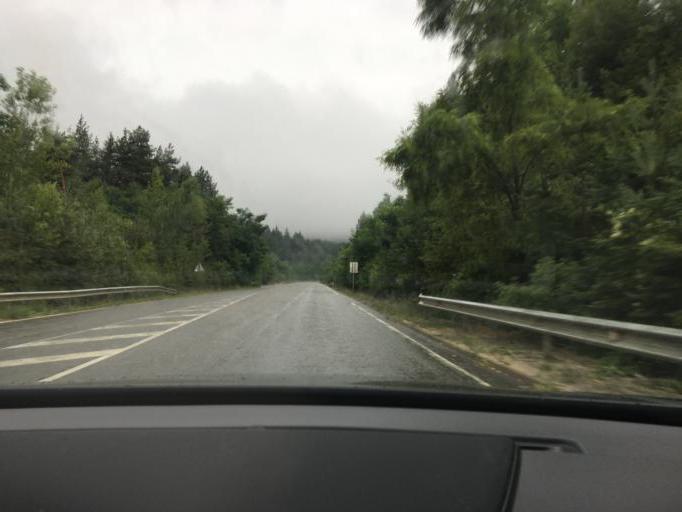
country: BG
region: Kyustendil
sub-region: Obshtina Kyustendil
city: Kyustendil
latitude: 42.2650
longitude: 22.5775
